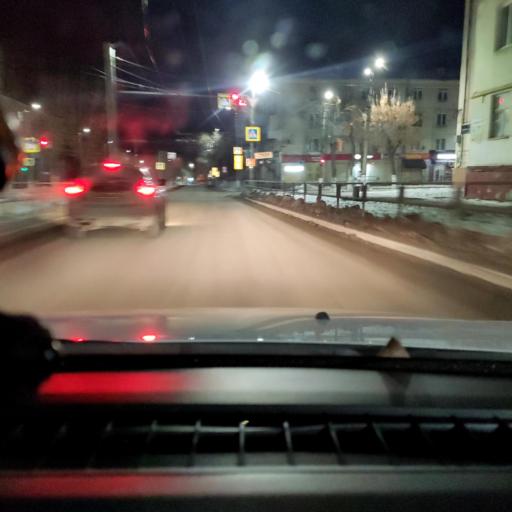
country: RU
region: Samara
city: Novokuybyshevsk
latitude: 53.0949
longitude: 49.9485
